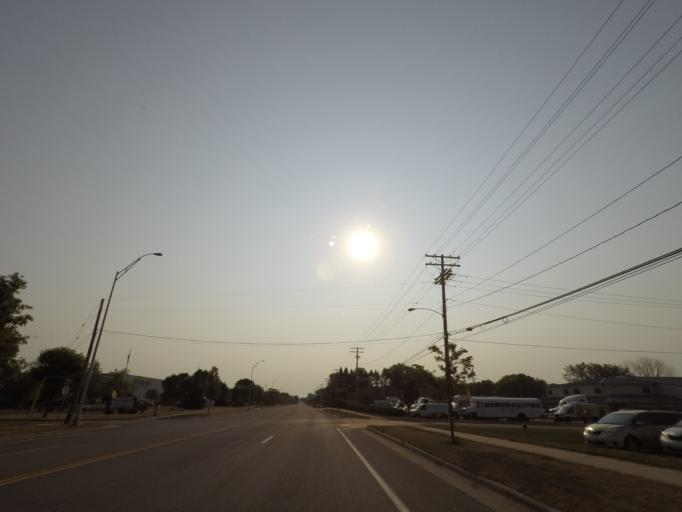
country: US
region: Wisconsin
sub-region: Dane County
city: McFarland
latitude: 43.0517
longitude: -89.2871
